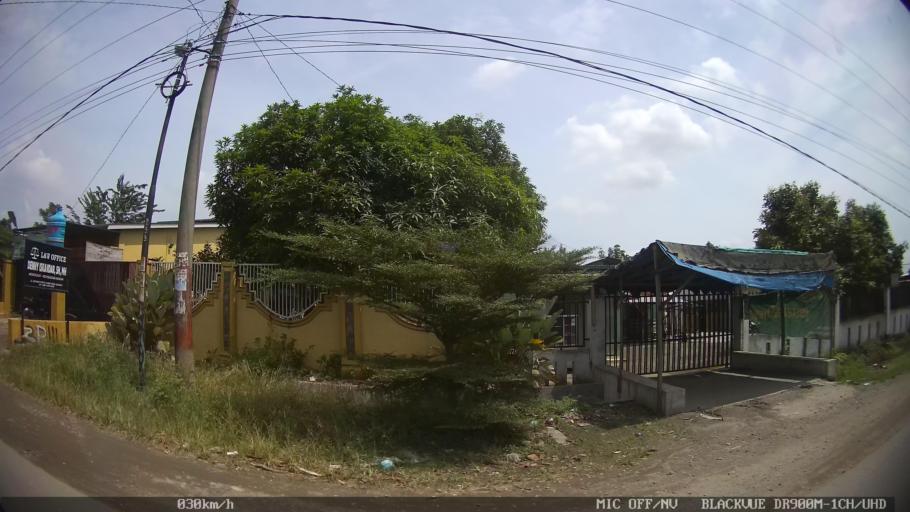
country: ID
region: North Sumatra
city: Medan
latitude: 3.6508
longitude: 98.7075
